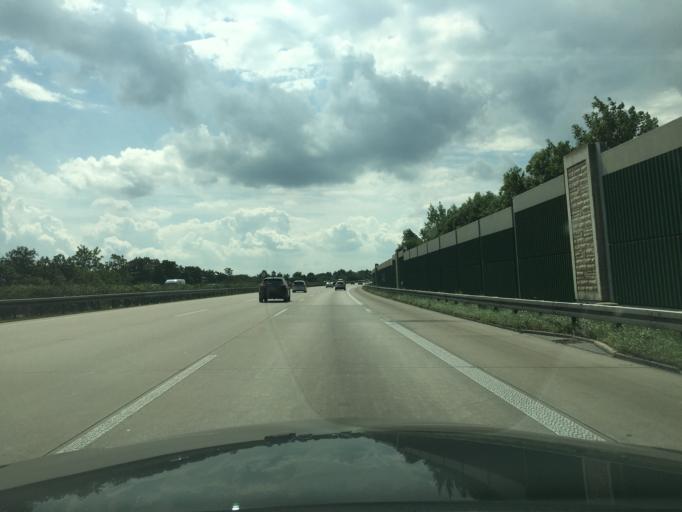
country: DE
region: Thuringia
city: Eisenberg
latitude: 50.9949
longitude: 11.9151
